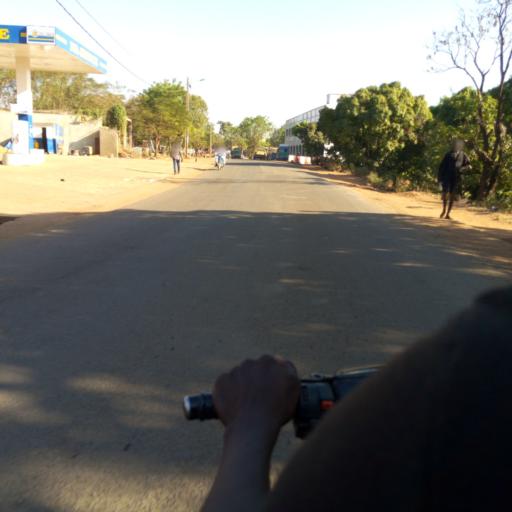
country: ML
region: Bamako
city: Bamako
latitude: 12.6590
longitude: -8.0323
